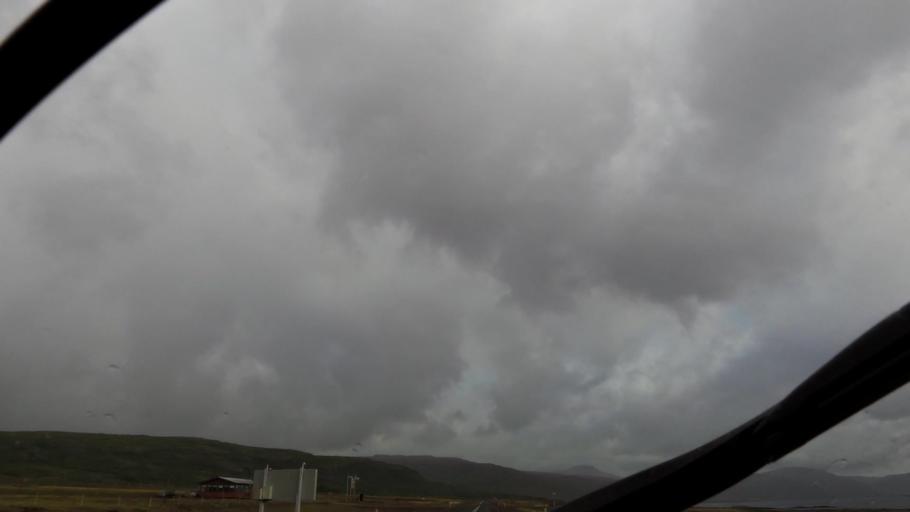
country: IS
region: Westfjords
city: Isafjoerdur
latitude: 65.5284
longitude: -23.1976
